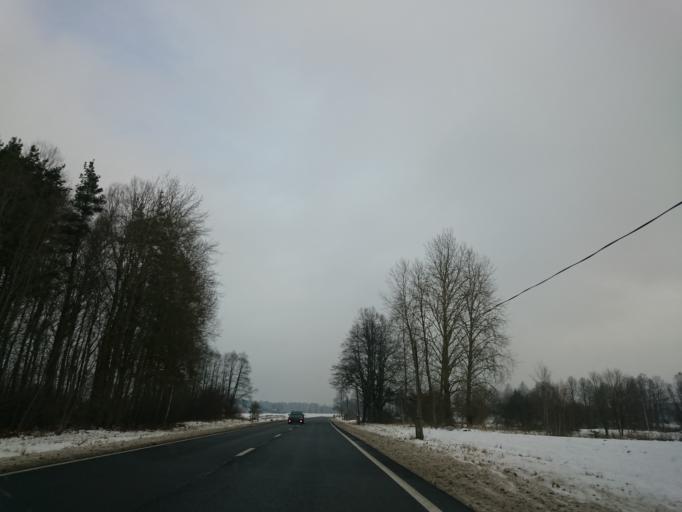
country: LV
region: Pargaujas
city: Stalbe
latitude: 57.3381
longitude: 24.9309
